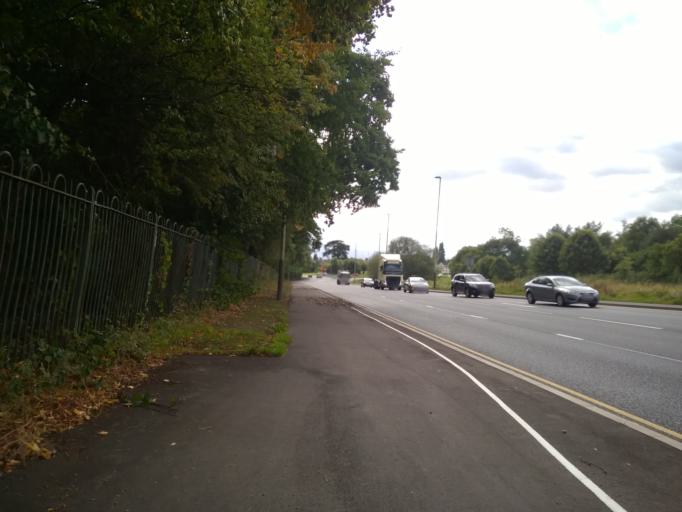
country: GB
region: England
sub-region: Leicestershire
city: Glenfield
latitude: 52.6550
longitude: -1.1752
